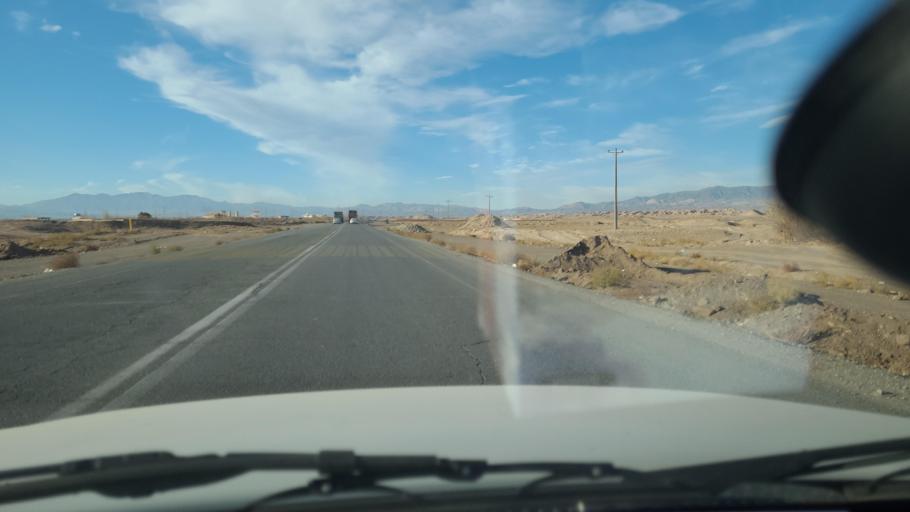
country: IR
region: Razavi Khorasan
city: Sabzevar
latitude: 36.2362
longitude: 57.6435
